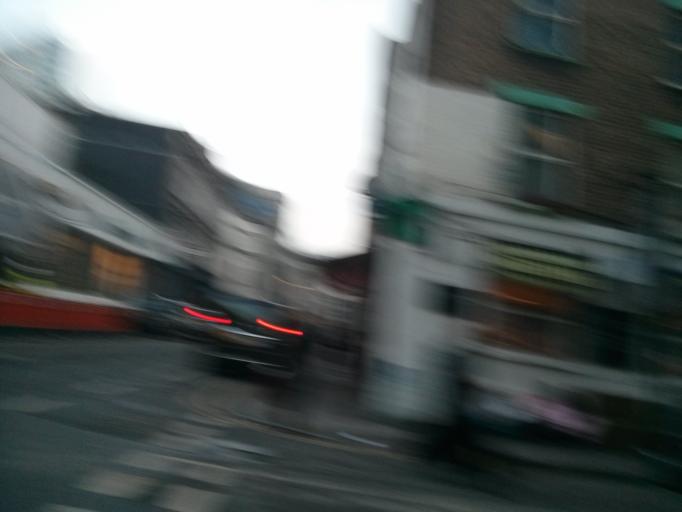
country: GB
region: England
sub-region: Greater London
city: Barbican
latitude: 51.5227
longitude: -0.0843
